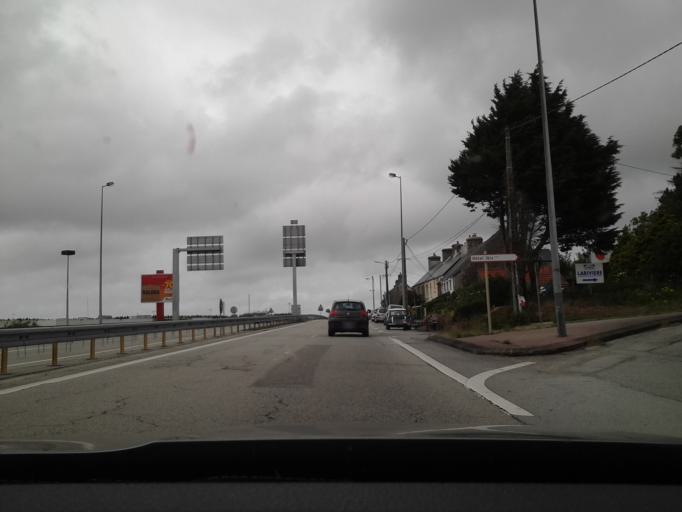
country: FR
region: Lower Normandy
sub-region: Departement de la Manche
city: La Glacerie
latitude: 49.6011
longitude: -1.5976
